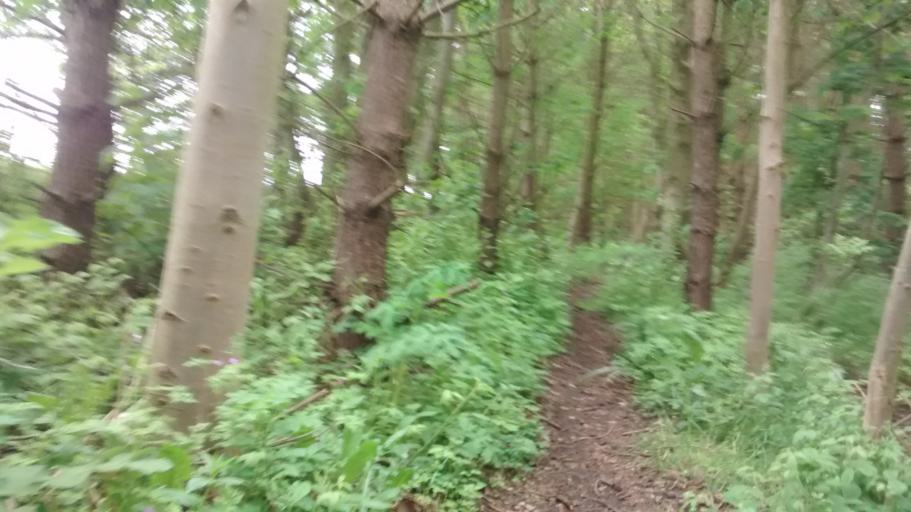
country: GB
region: England
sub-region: County Durham
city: Pittington
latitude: 54.7869
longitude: -1.4785
